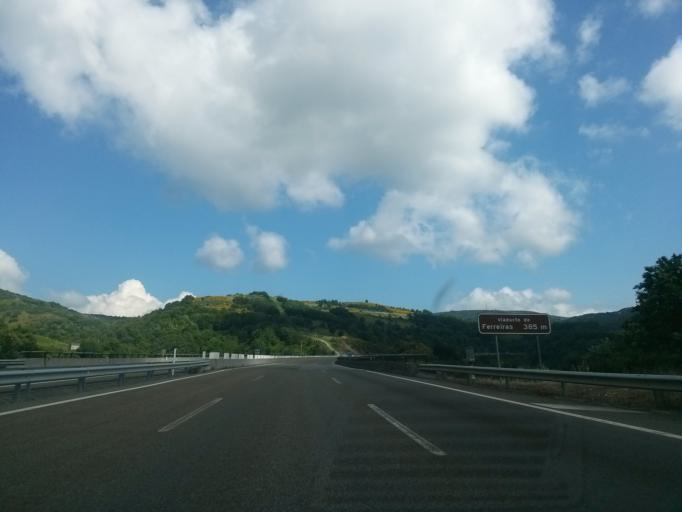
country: ES
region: Galicia
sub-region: Provincia de Lugo
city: San Roman
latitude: 42.7439
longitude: -7.0527
